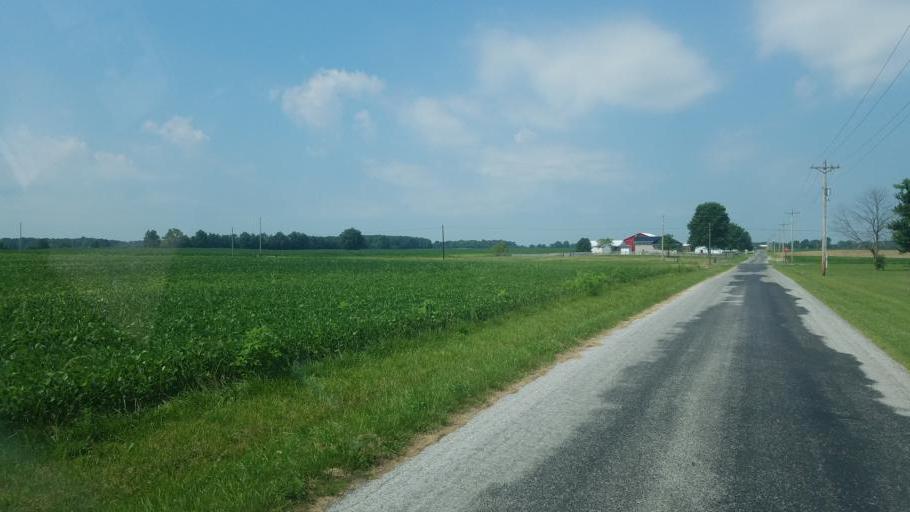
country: US
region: Ohio
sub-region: Union County
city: Richwood
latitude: 40.5469
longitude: -83.3878
